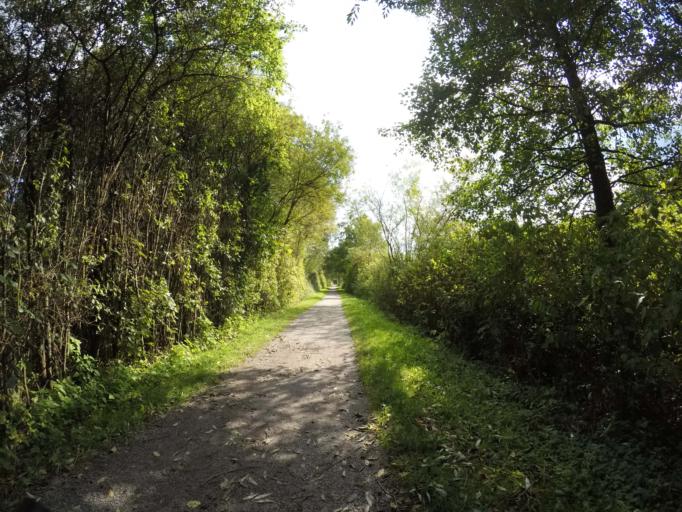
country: DE
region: North Rhine-Westphalia
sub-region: Regierungsbezirk Detmold
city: Hiddenhausen
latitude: 52.1377
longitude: 8.6344
